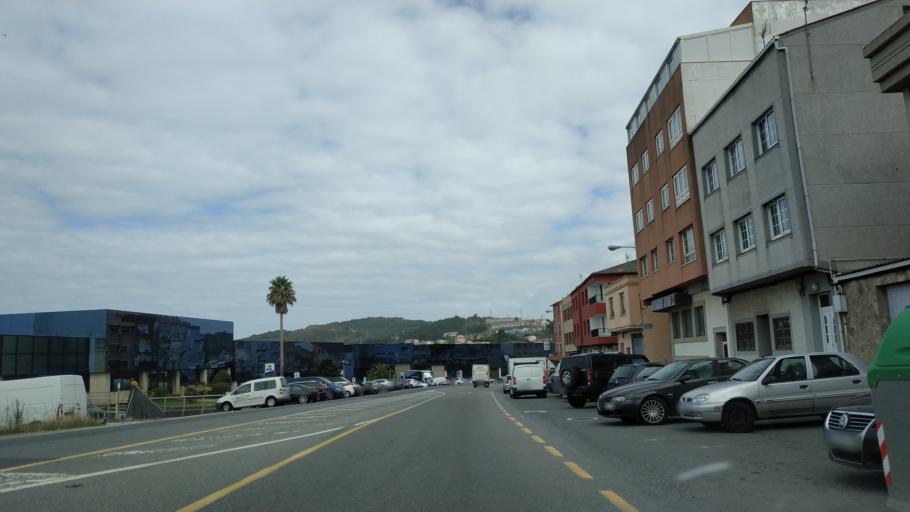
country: ES
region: Galicia
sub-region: Provincia da Coruna
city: Arteixo
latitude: 43.3152
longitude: -8.4993
